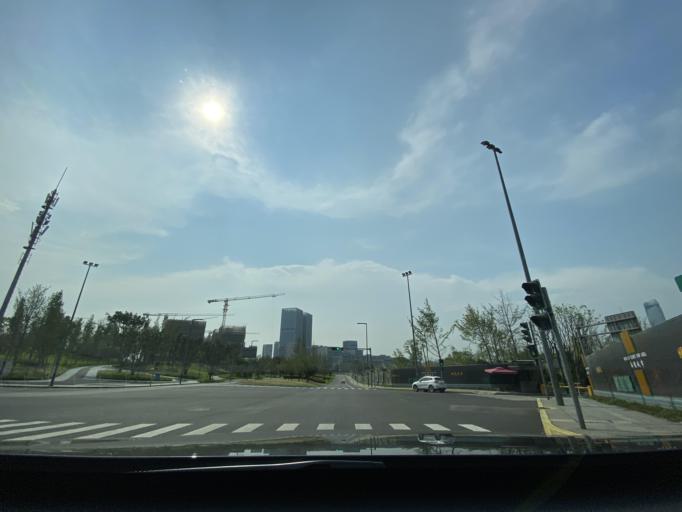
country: CN
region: Sichuan
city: Dongsheng
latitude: 30.3941
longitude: 104.0780
